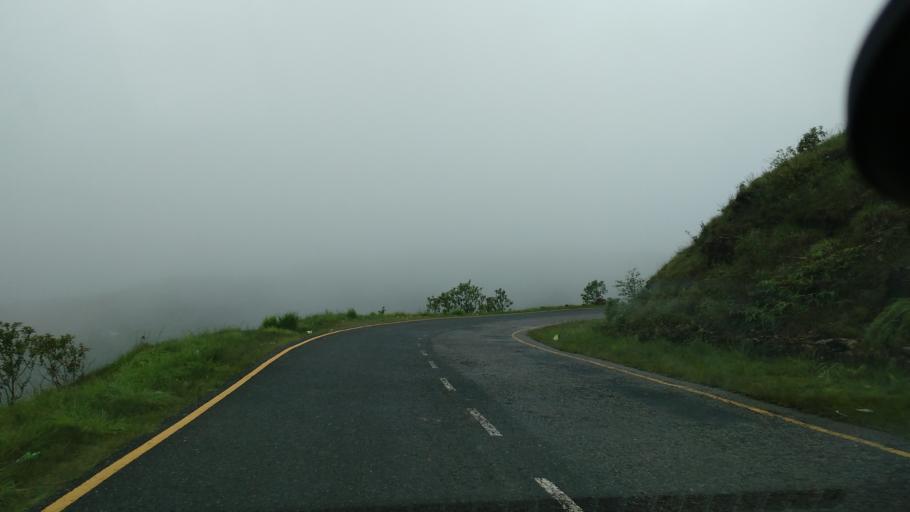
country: IN
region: Meghalaya
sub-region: East Khasi Hills
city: Cherrapunji
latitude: 25.3166
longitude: 91.7323
